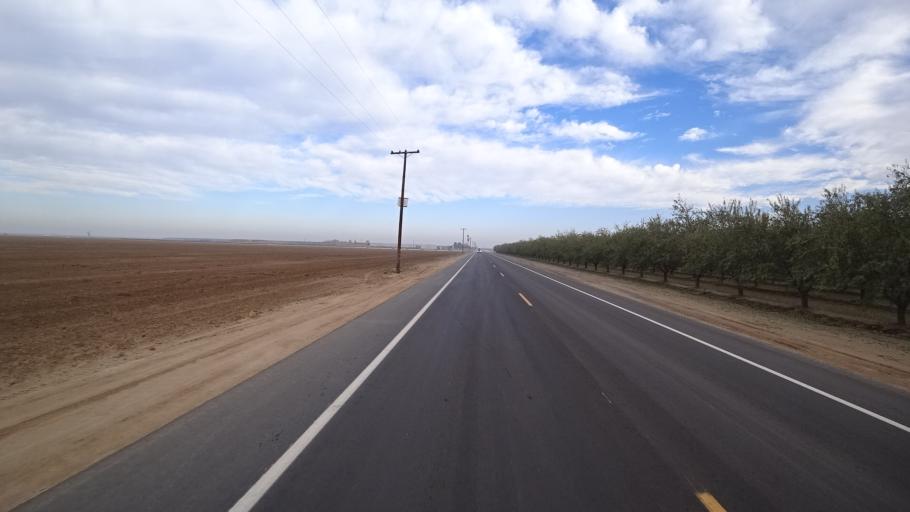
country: US
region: California
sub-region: Kern County
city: Rosedale
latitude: 35.4097
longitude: -119.1988
